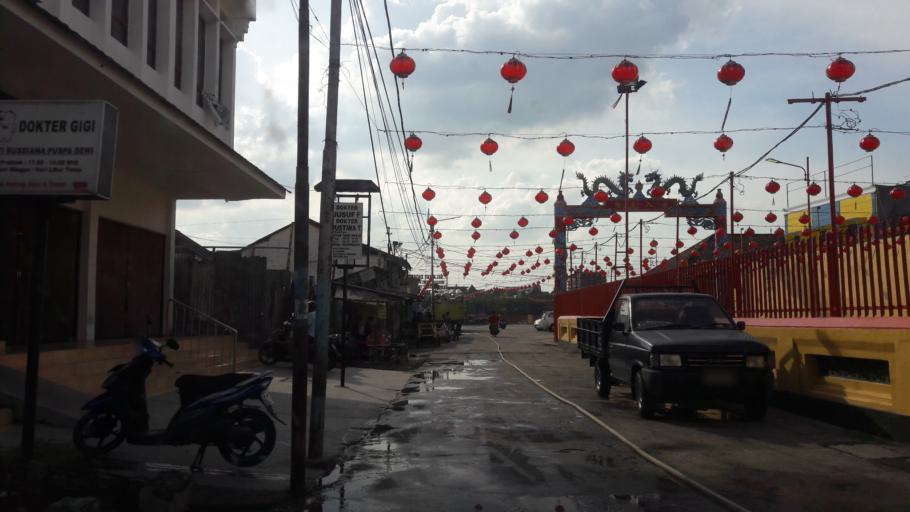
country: ID
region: South Sumatra
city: Plaju
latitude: -2.9924
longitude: 104.7662
